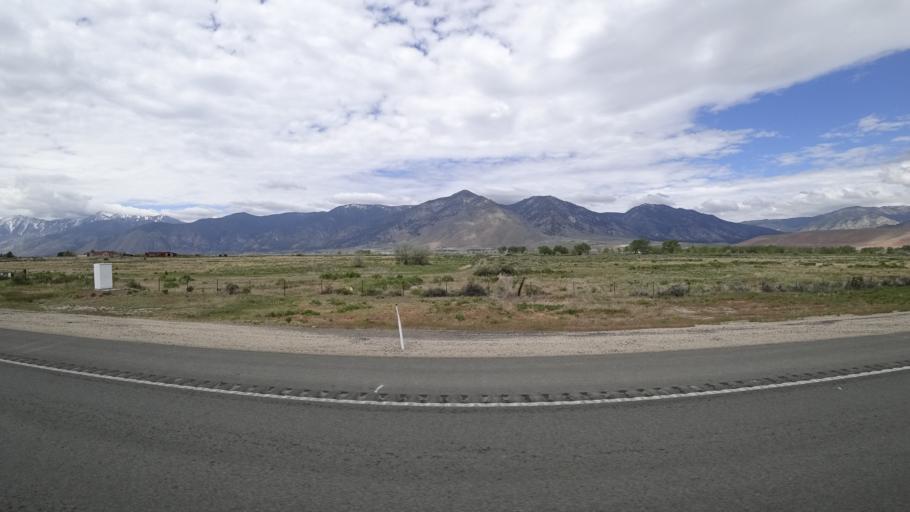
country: US
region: Nevada
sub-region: Douglas County
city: Indian Hills
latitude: 39.0419
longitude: -119.7800
